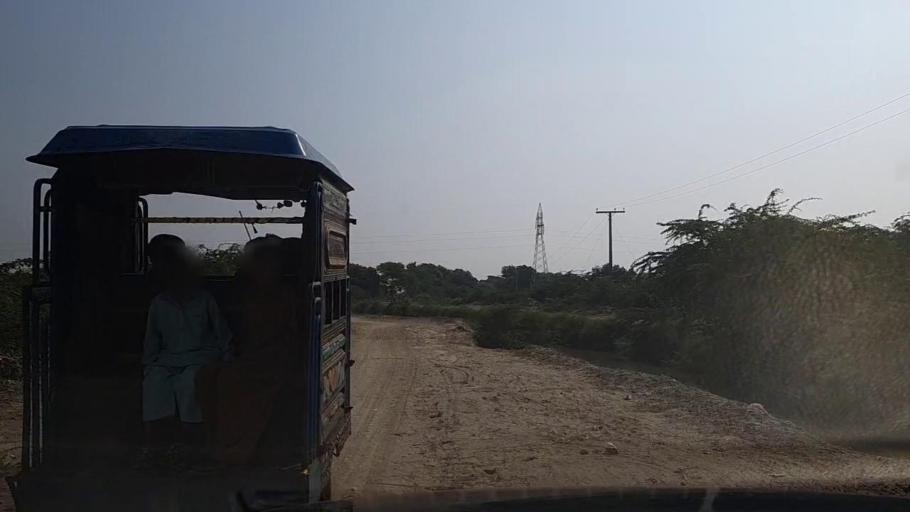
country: PK
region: Sindh
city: Mirpur Batoro
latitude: 24.7030
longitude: 68.2170
